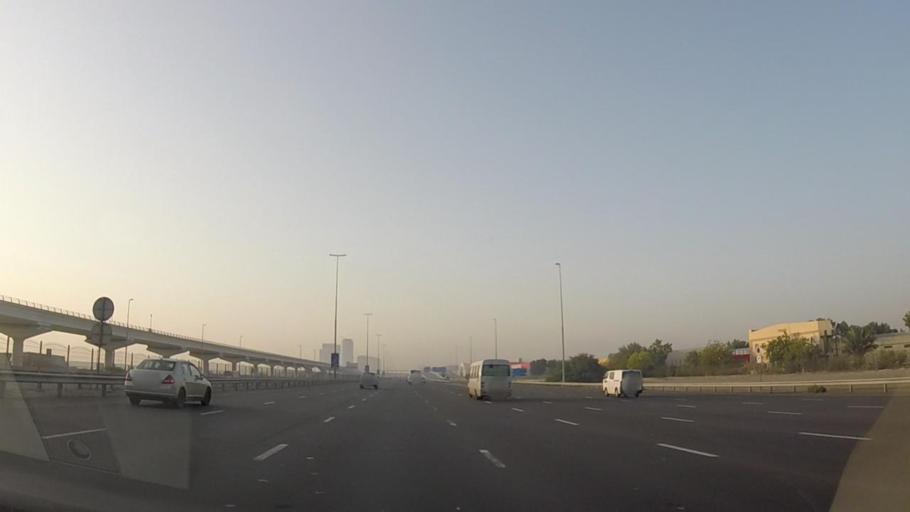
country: AE
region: Dubai
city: Dubai
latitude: 25.0005
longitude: 55.0950
